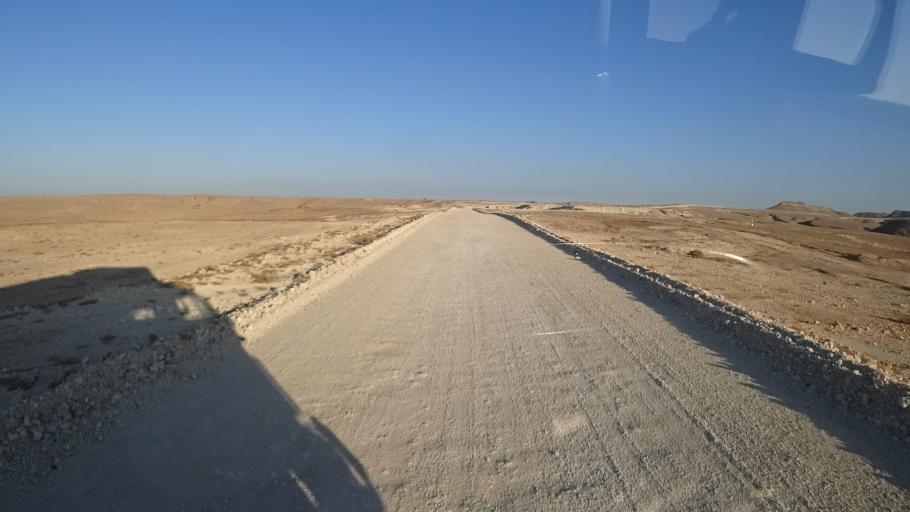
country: YE
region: Al Mahrah
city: Hawf
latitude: 17.1540
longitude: 53.3519
